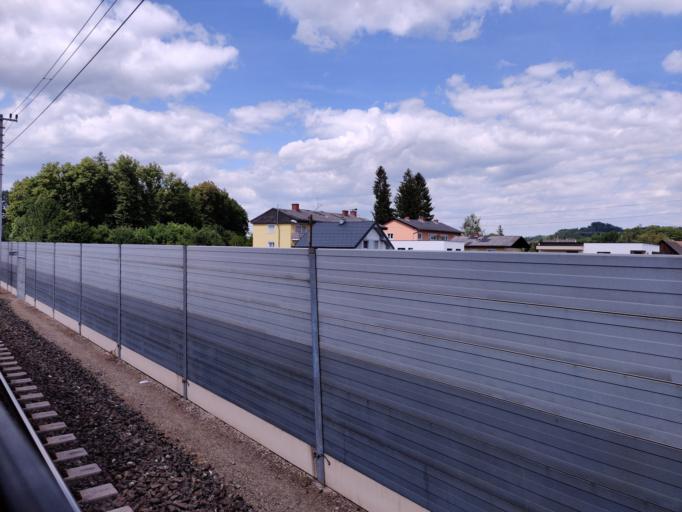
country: AT
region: Styria
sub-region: Politischer Bezirk Leibnitz
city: Weitendorf
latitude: 46.9091
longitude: 15.4778
